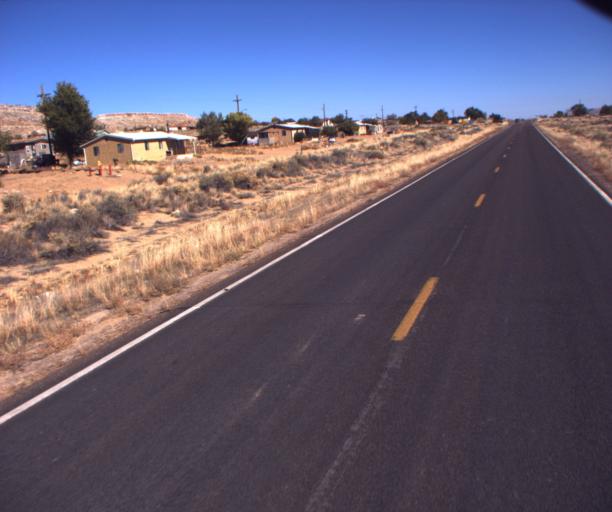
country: US
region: Arizona
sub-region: Navajo County
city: First Mesa
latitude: 35.8216
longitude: -110.3951
